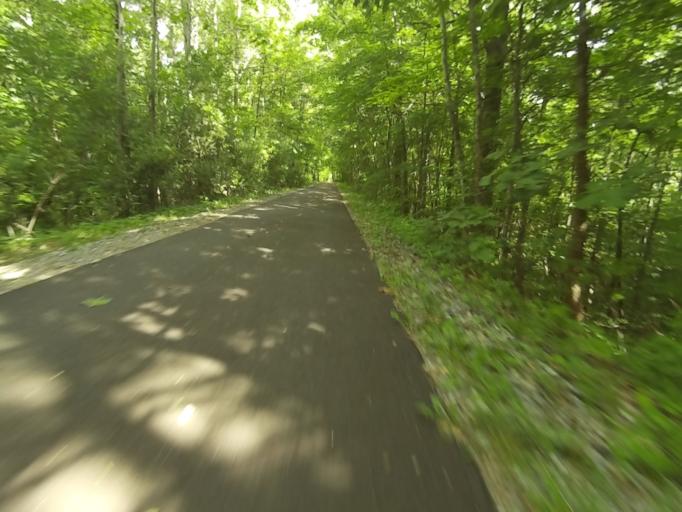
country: US
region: Ohio
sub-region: Summit County
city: Boston Heights
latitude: 41.2486
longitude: -81.5141
